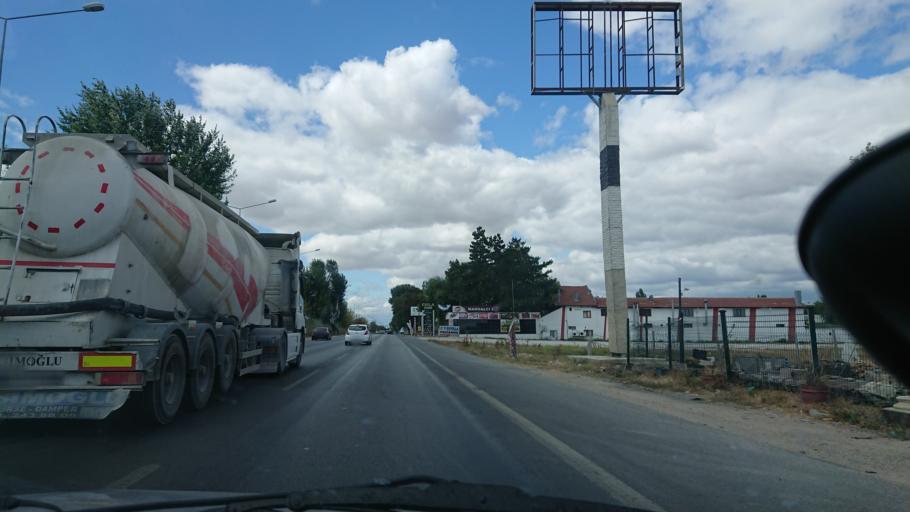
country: TR
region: Eskisehir
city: Eskisehir
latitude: 39.8025
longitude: 30.4283
